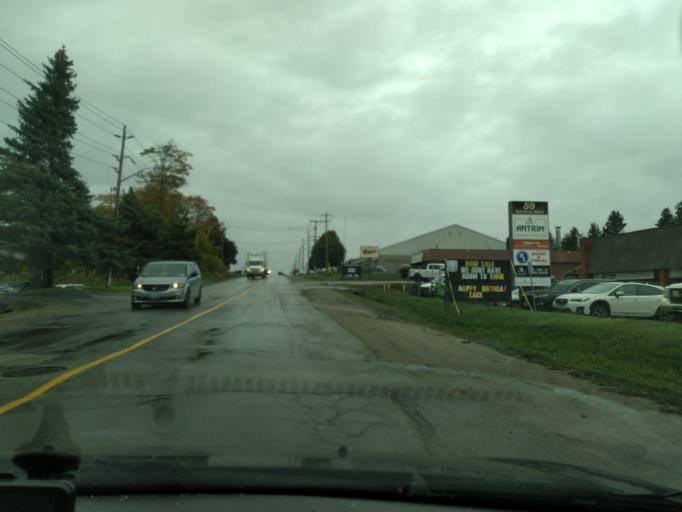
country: CA
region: Ontario
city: Barrie
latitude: 44.4088
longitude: -79.6805
